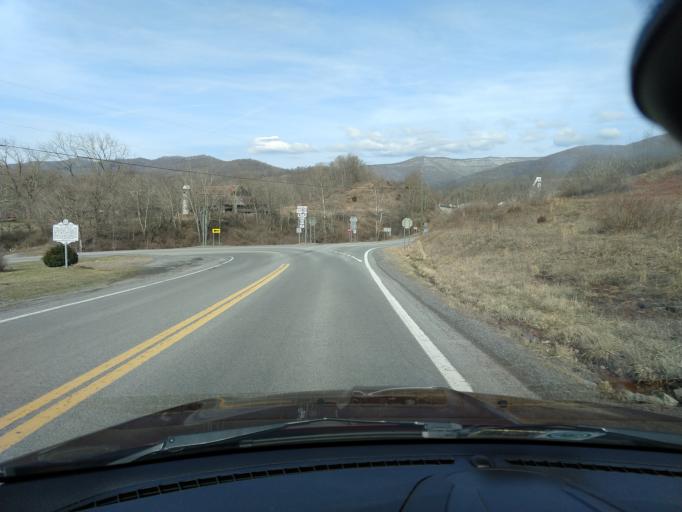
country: US
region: West Virginia
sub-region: Pocahontas County
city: Marlinton
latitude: 38.1579
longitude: -80.1801
